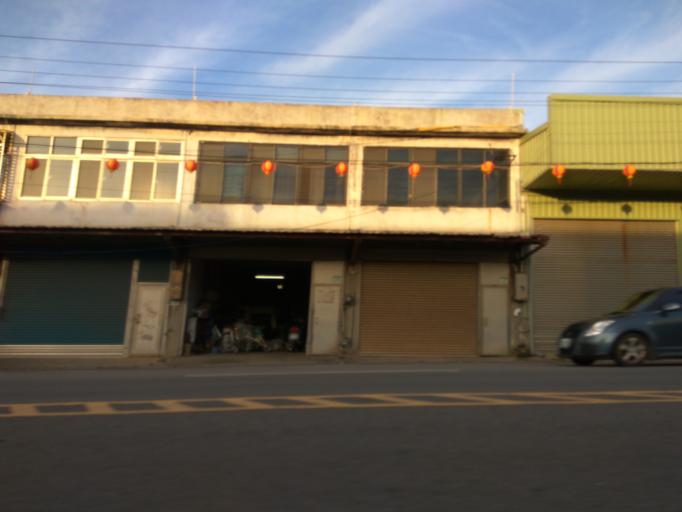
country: TW
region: Taiwan
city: Taoyuan City
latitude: 25.0054
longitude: 121.1486
